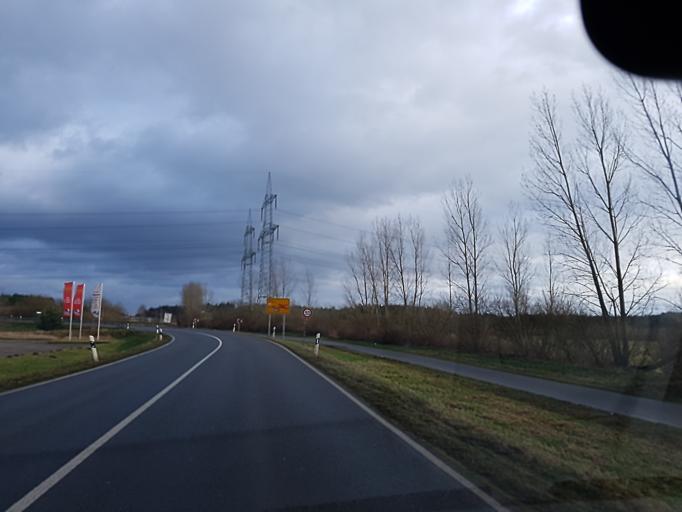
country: DE
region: Brandenburg
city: Bad Liebenwerda
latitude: 51.5139
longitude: 13.4246
